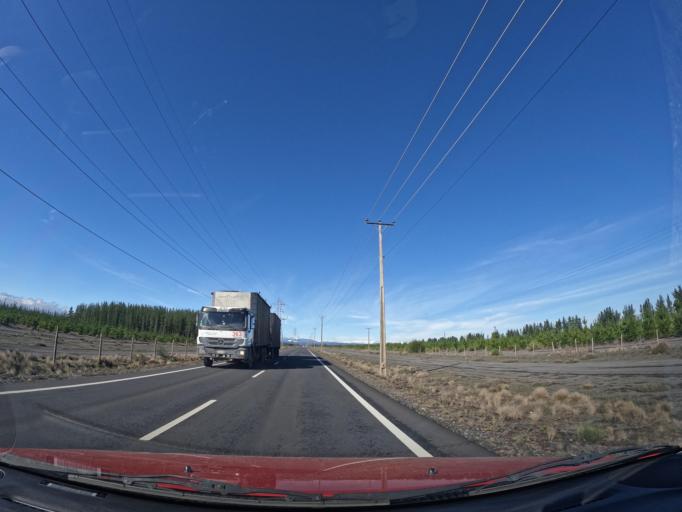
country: CL
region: Biobio
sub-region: Provincia de Biobio
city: Los Angeles
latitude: -37.2113
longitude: -72.0115
